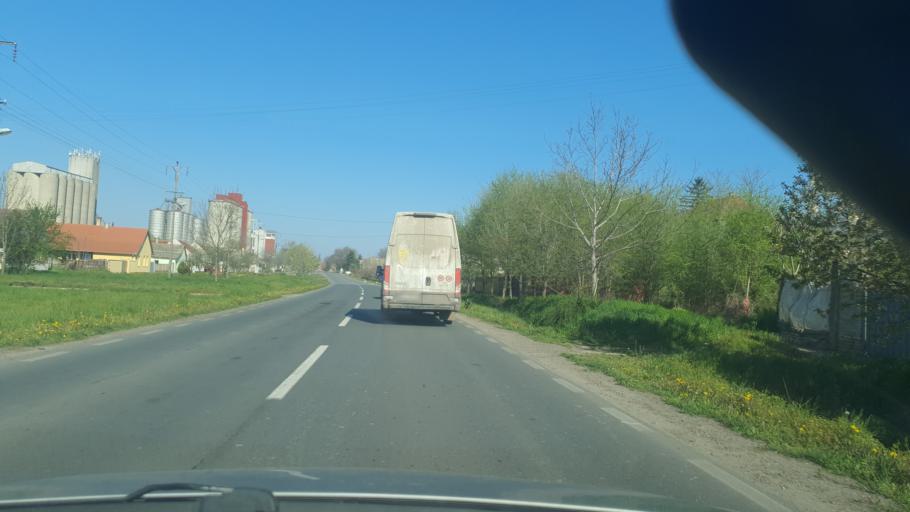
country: RS
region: Autonomna Pokrajina Vojvodina
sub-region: Zapadnobacki Okrug
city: Kula
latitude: 45.6899
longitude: 19.3868
